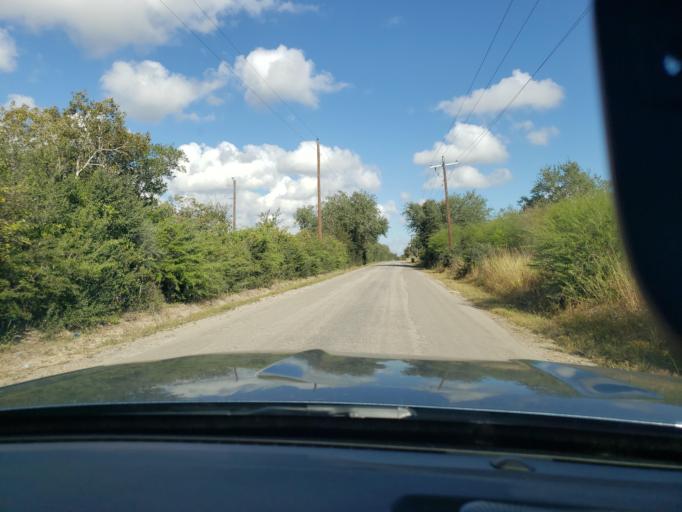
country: US
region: Texas
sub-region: Bee County
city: Beeville
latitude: 28.4435
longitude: -97.7146
